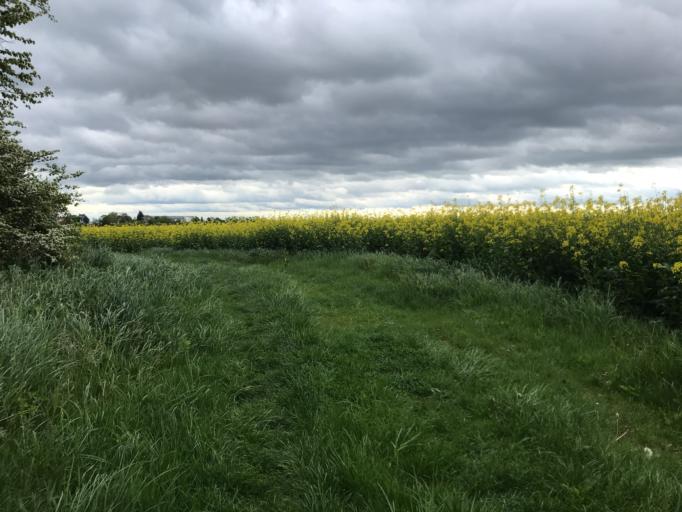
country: DE
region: Rheinland-Pfalz
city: Ober-Olm
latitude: 49.9489
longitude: 8.1797
